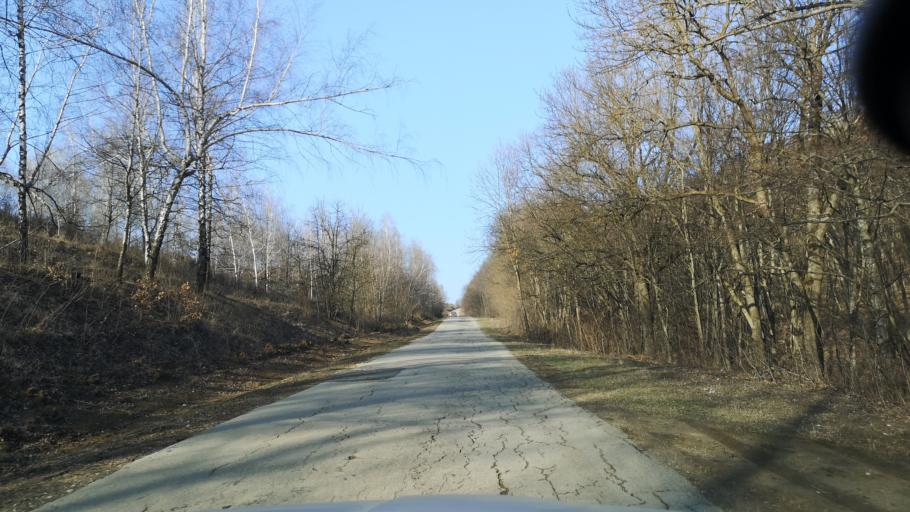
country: MD
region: Nisporeni
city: Nisporeni
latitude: 47.0960
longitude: 28.3155
